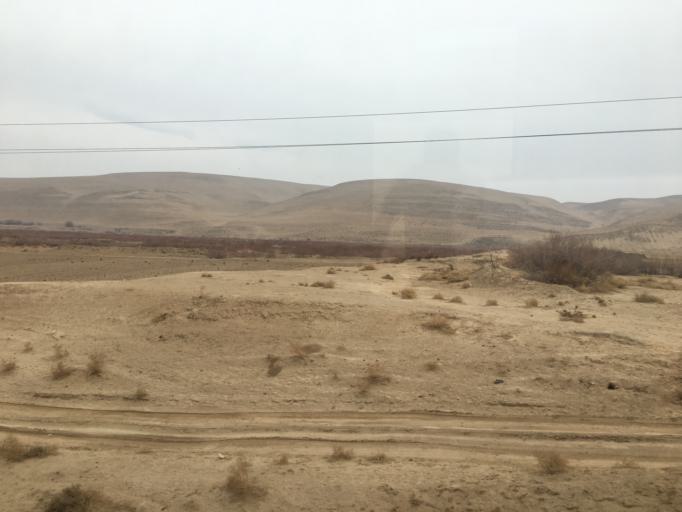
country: AF
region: Badghis
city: Bala Murghab
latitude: 35.9312
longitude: 62.7161
